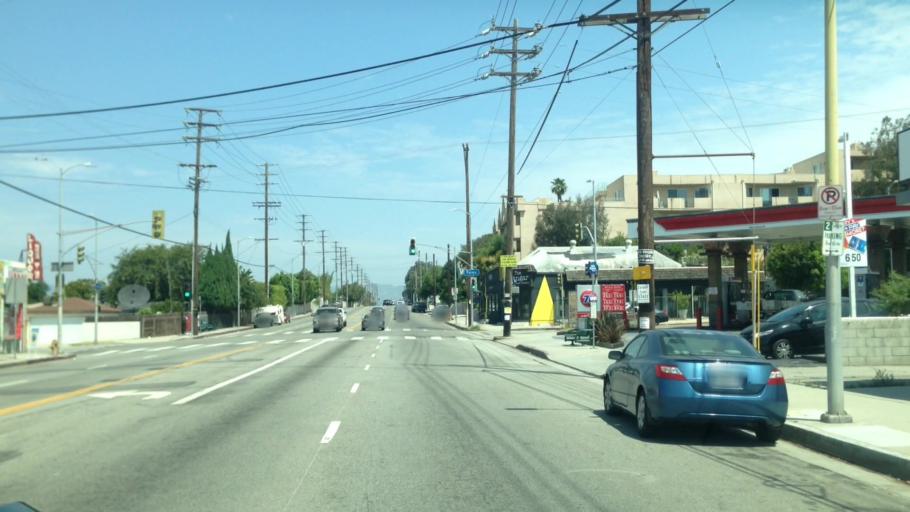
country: US
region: California
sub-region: Los Angeles County
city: Marina del Rey
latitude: 34.0101
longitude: -118.4384
